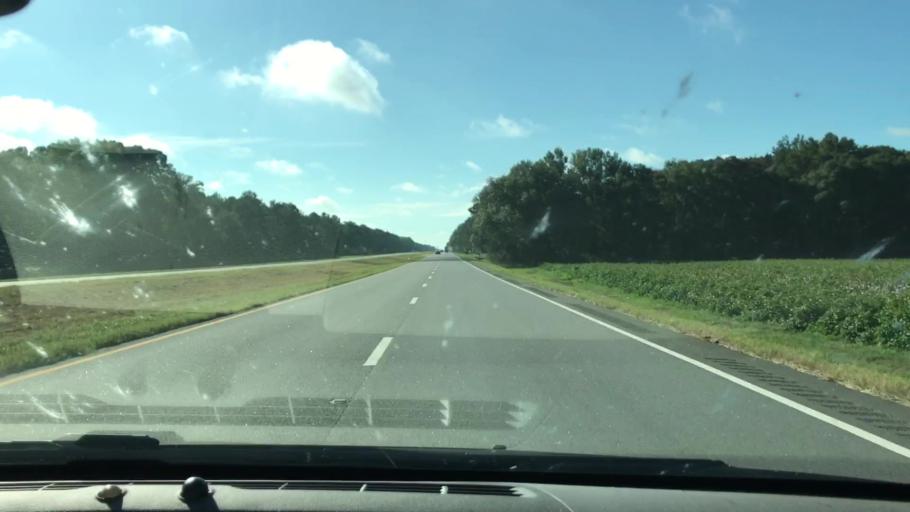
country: US
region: Georgia
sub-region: Lee County
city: Leesburg
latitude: 31.6876
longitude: -84.3087
